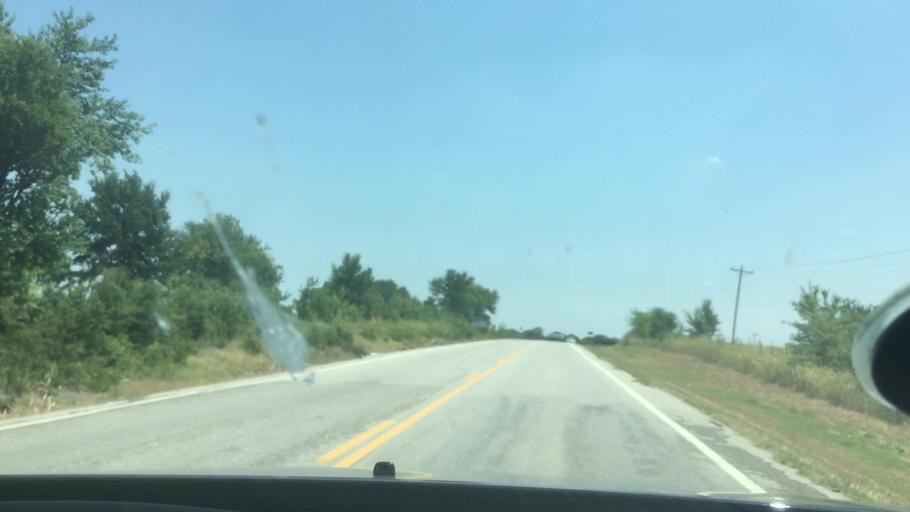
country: US
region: Oklahoma
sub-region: Bryan County
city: Durant
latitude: 34.1492
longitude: -96.3770
